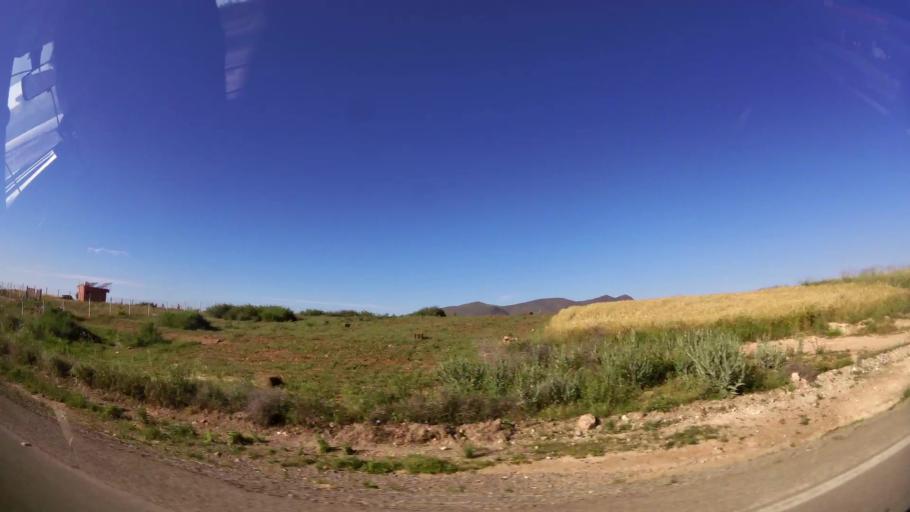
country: MA
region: Oriental
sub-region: Berkane-Taourirt
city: Ahfir
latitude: 34.9772
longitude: -2.1325
